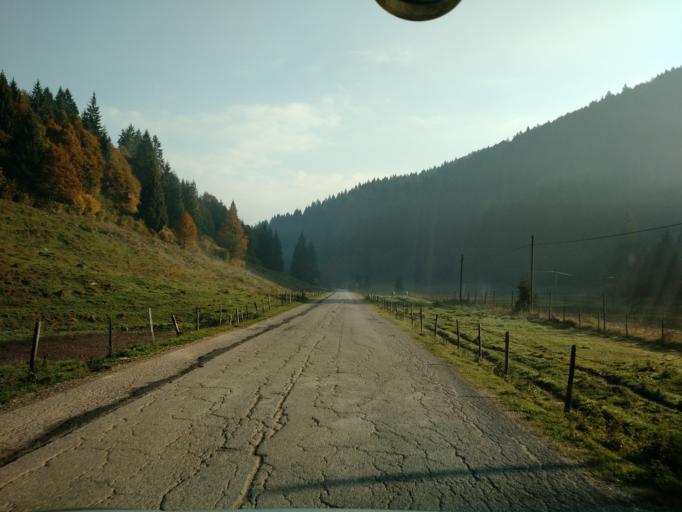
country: IT
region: Veneto
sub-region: Provincia di Vicenza
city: Conco
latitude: 45.8373
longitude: 11.5879
